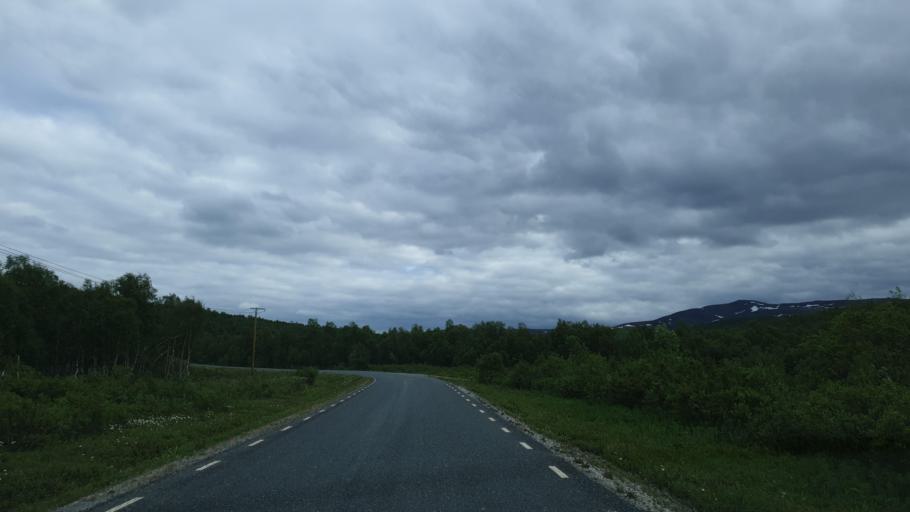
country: NO
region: Nordland
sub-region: Hattfjelldal
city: Hattfjelldal
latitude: 65.4235
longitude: 14.6608
